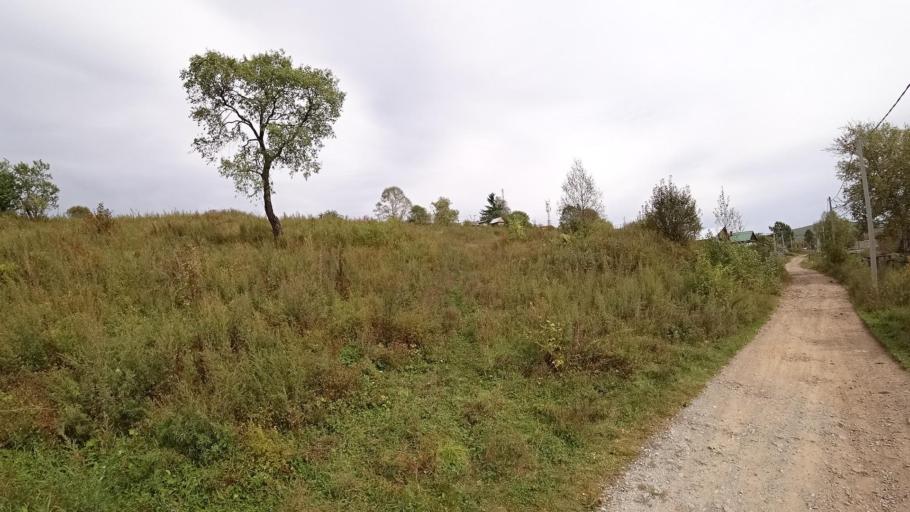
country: RU
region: Jewish Autonomous Oblast
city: Khingansk
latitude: 49.1277
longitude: 131.2015
